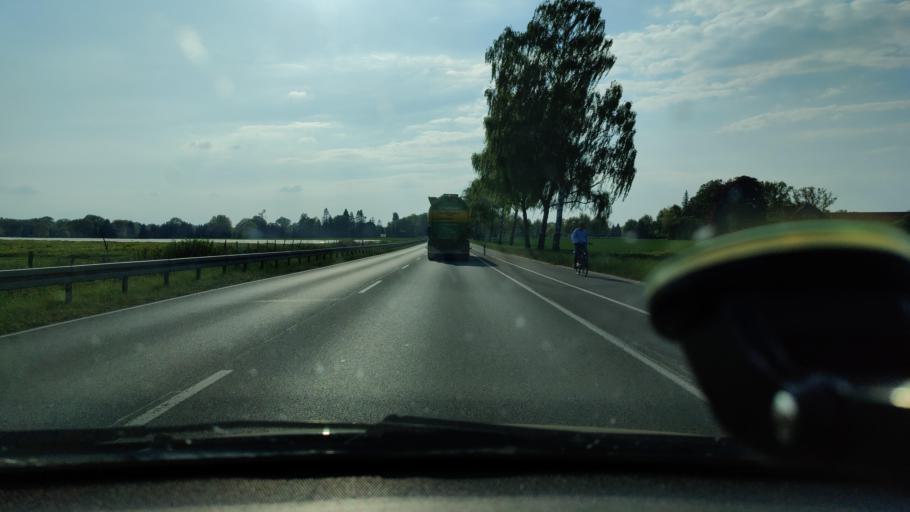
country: DE
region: North Rhine-Westphalia
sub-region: Regierungsbezirk Munster
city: Telgte
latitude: 51.9828
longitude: 7.7573
